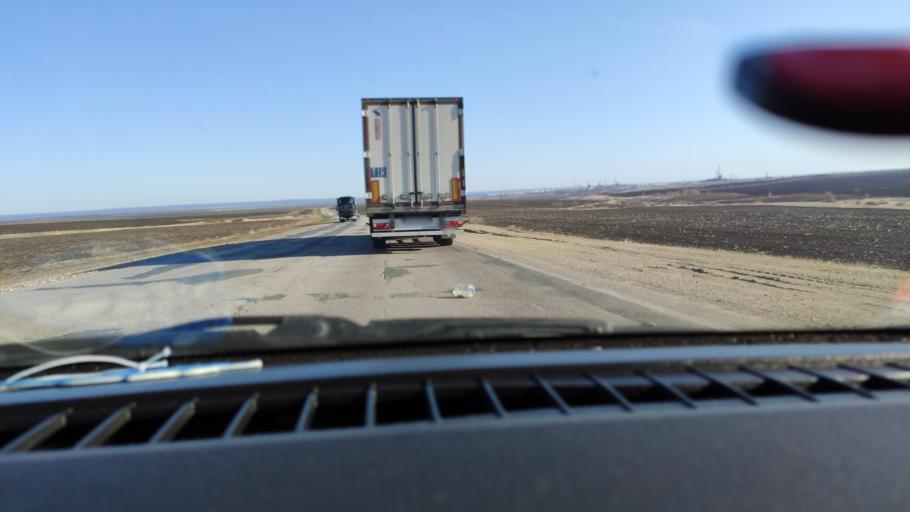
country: RU
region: Samara
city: Syzran'
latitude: 53.0061
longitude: 48.3323
